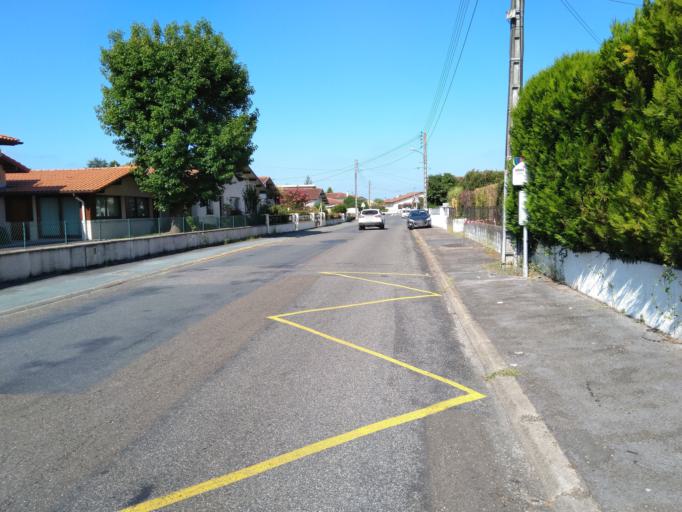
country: FR
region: Aquitaine
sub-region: Departement des Landes
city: Saint-Paul-les-Dax
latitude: 43.7294
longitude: -1.0533
